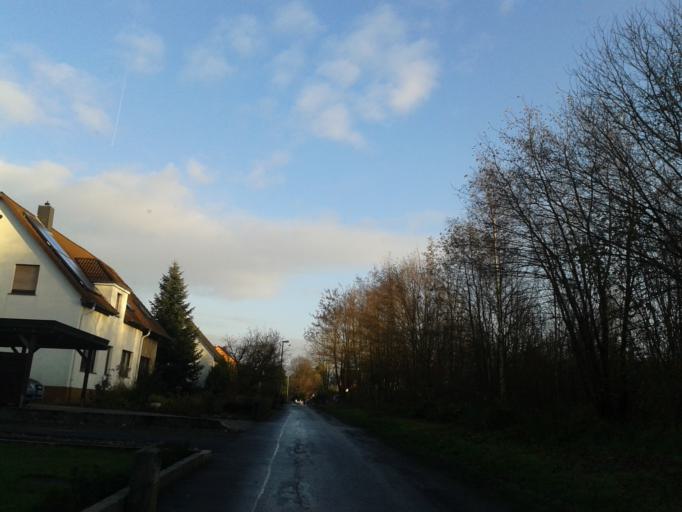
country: DE
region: North Rhine-Westphalia
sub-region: Regierungsbezirk Detmold
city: Detmold
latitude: 51.9533
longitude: 8.8266
